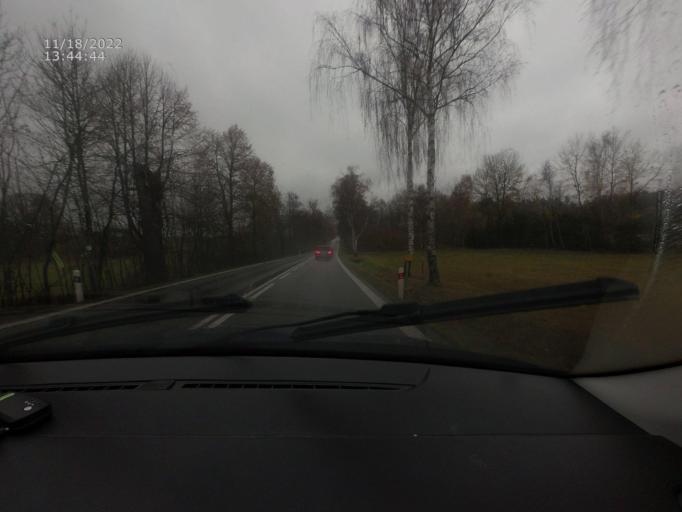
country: CZ
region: Jihocesky
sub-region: Okres Strakonice
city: Blatna
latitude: 49.4304
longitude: 13.8343
